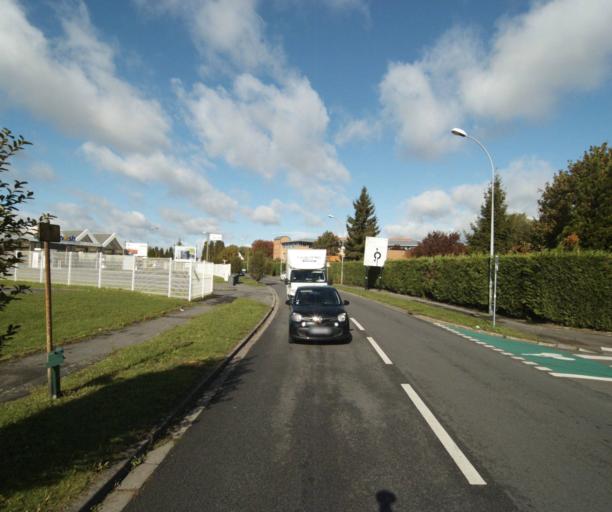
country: FR
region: Nord-Pas-de-Calais
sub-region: Departement du Nord
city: Lomme
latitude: 50.6448
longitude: 3.0060
